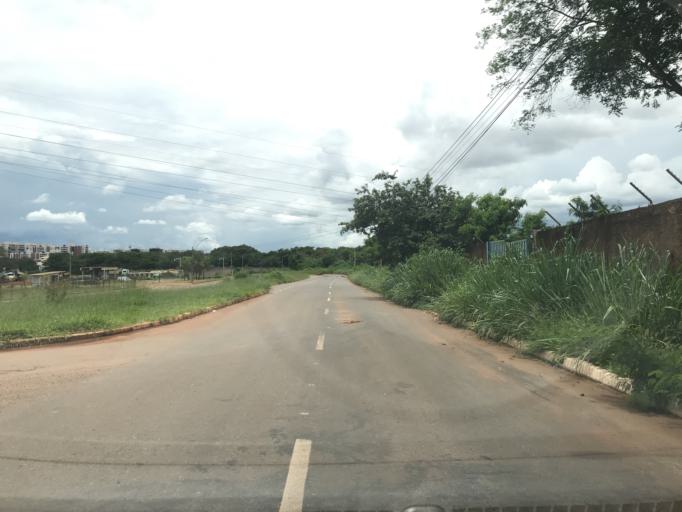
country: BR
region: Federal District
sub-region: Brasilia
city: Brasilia
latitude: -15.8142
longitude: -47.9587
